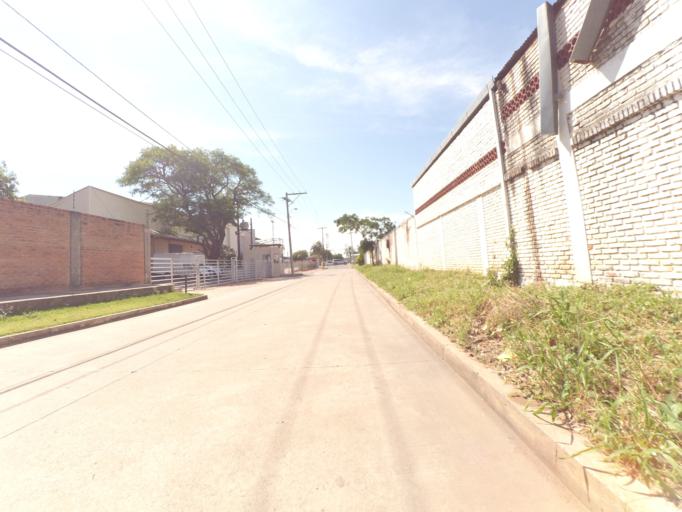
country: BO
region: Santa Cruz
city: Santa Cruz de la Sierra
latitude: -17.8098
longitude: -63.2075
